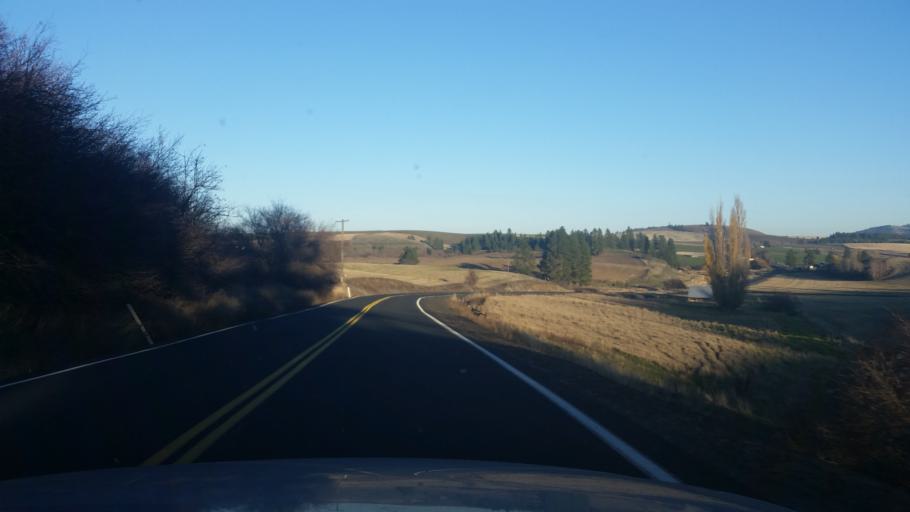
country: US
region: Washington
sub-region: Spokane County
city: Opportunity
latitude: 47.3526
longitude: -117.2609
